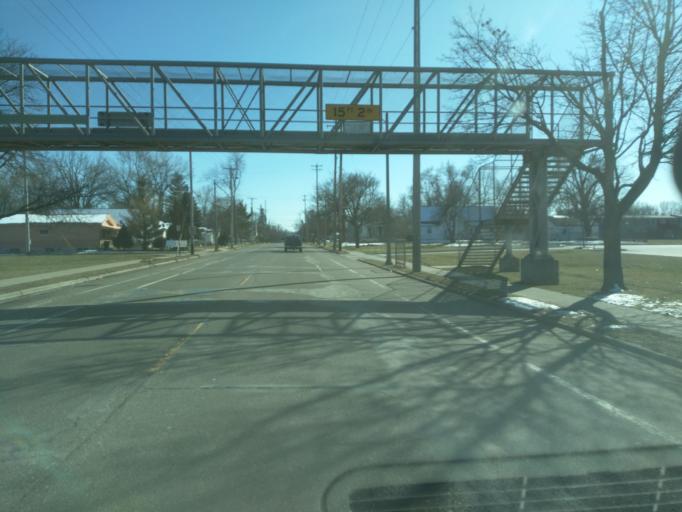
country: US
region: Michigan
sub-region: Ingham County
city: Lansing
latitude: 42.6888
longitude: -84.5824
